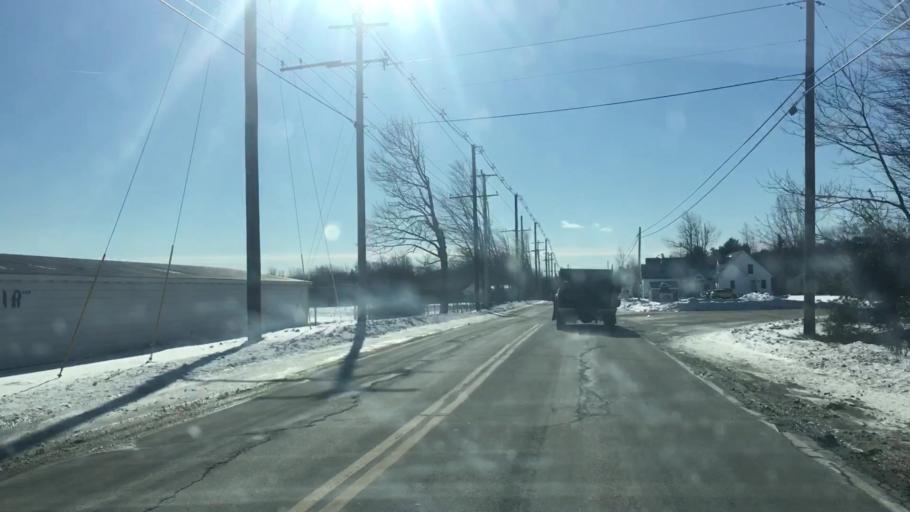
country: US
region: Maine
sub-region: Hancock County
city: Surry
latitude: 44.4315
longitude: -68.5748
